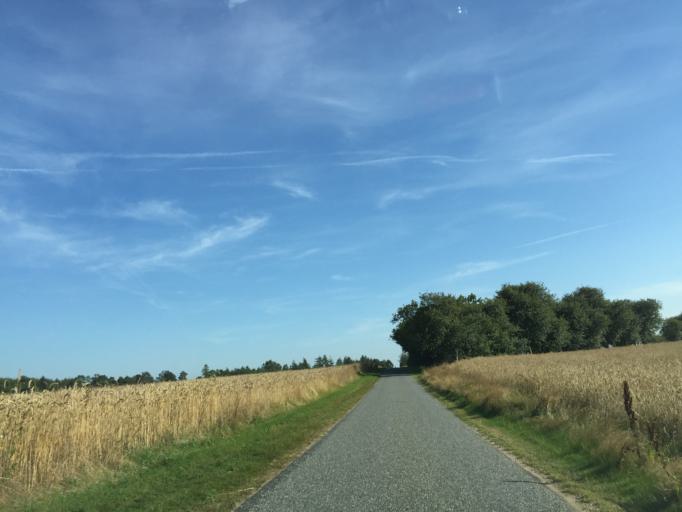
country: DK
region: Central Jutland
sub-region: Viborg Kommune
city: Bjerringbro
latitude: 56.2808
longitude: 9.6903
